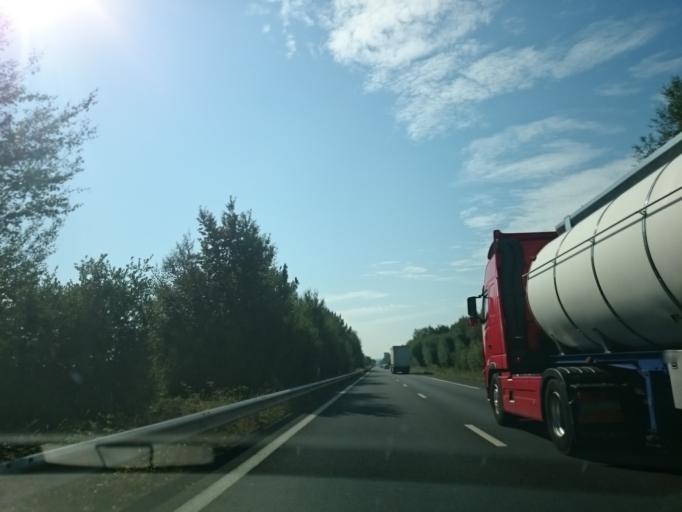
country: FR
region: Pays de la Loire
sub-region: Departement de la Loire-Atlantique
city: Jans
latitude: 47.6322
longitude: -1.6485
